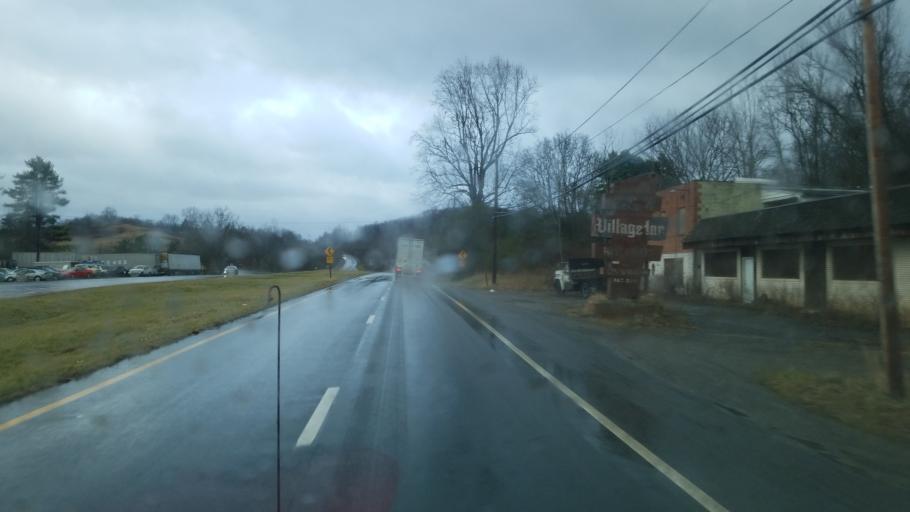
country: US
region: Virginia
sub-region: Giles County
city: Pearisburg
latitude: 37.3079
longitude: -80.7359
